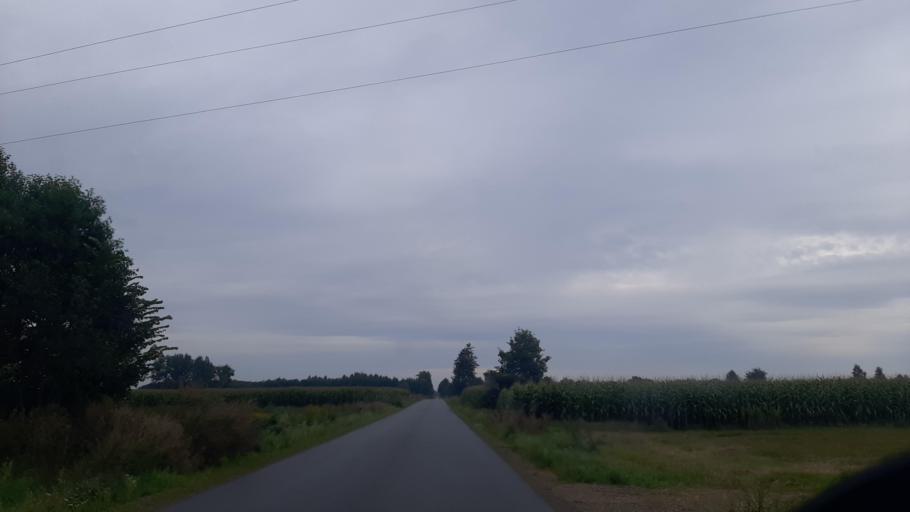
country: PL
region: Lublin Voivodeship
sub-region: Powiat lubartowski
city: Kamionka
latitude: 51.4680
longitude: 22.4381
